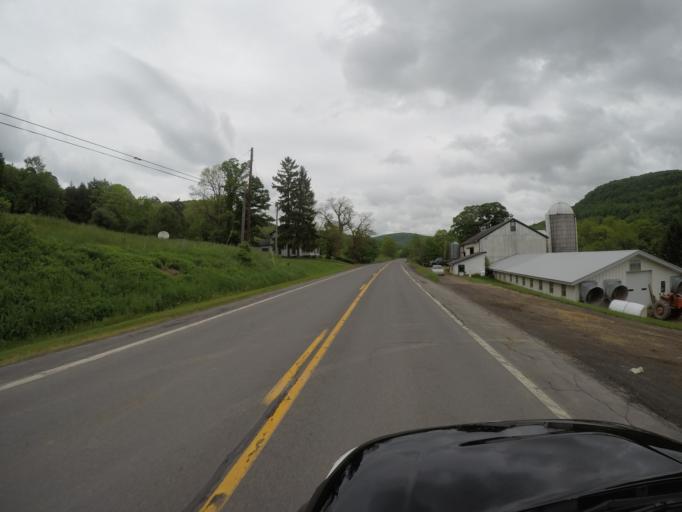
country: US
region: New York
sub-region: Delaware County
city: Delhi
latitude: 42.2576
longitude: -74.8862
